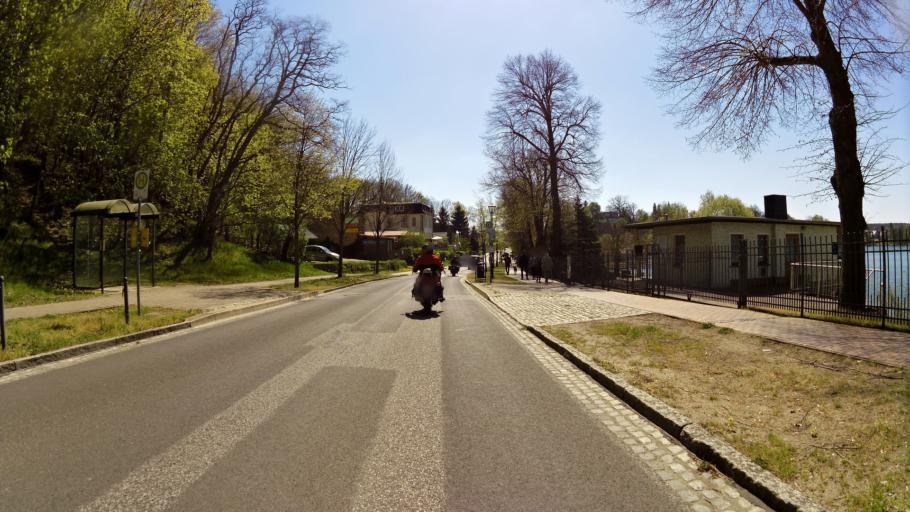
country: DE
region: Brandenburg
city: Buckow
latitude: 52.5749
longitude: 14.0703
